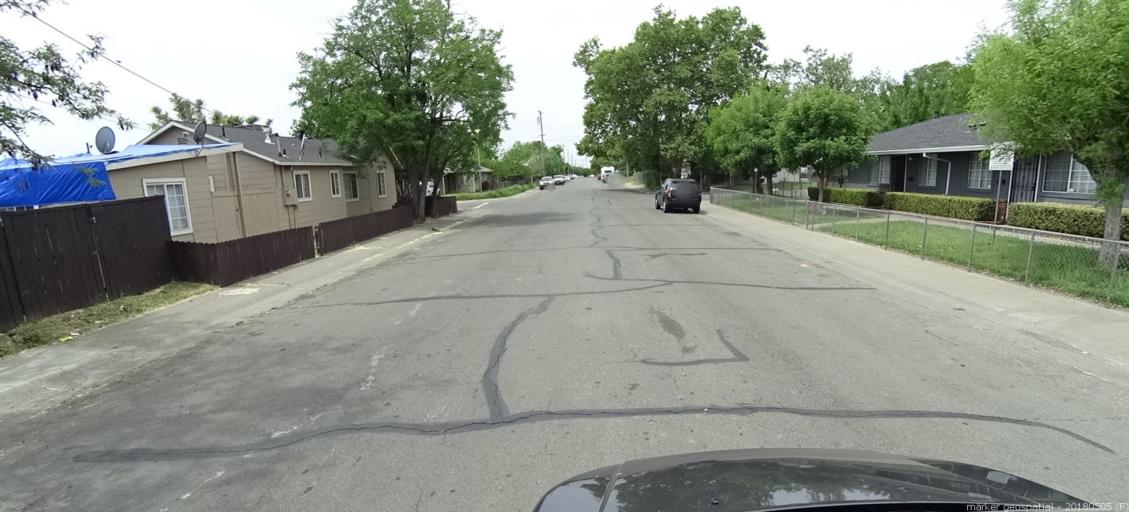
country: US
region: California
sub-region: Sacramento County
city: Rio Linda
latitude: 38.6384
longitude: -121.4402
